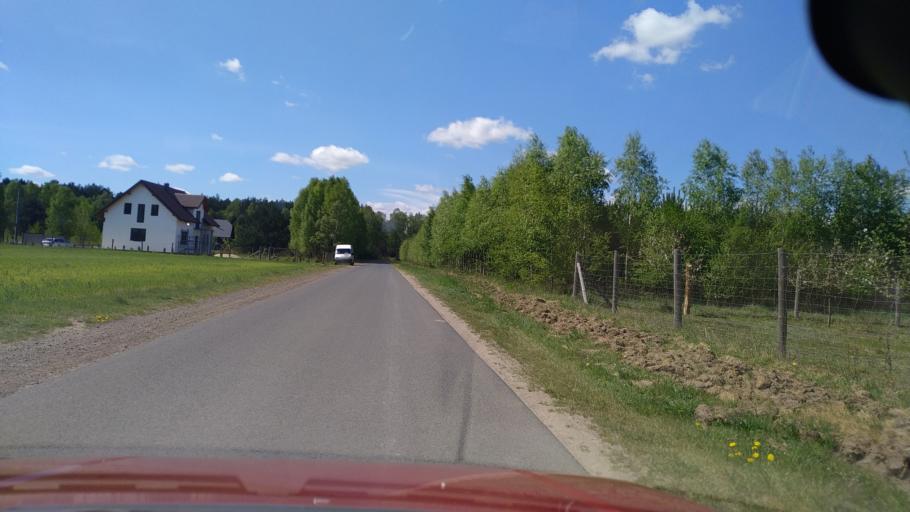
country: PL
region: Greater Poland Voivodeship
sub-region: Powiat zlotowski
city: Tarnowka
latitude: 53.2650
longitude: 16.8995
